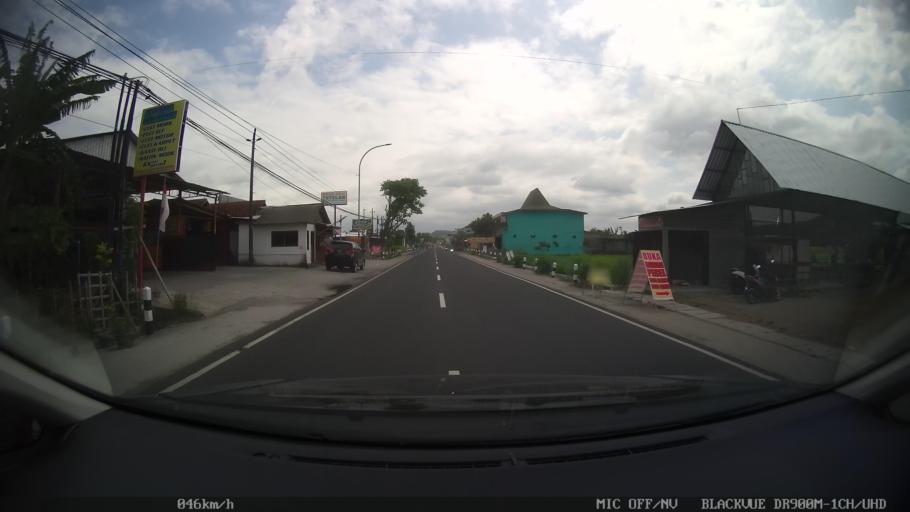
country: ID
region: Central Java
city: Candi Prambanan
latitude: -7.7981
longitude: 110.4828
